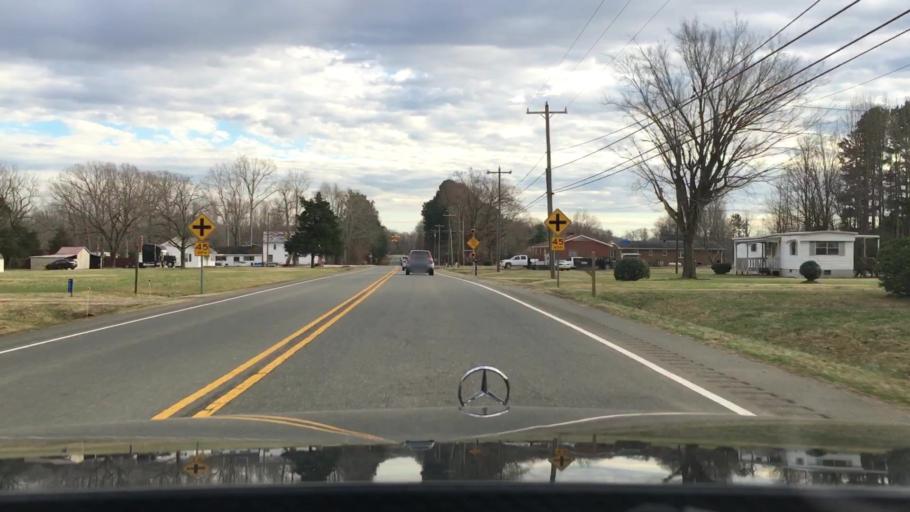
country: US
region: North Carolina
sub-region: Orange County
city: Hillsborough
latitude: 36.1766
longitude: -79.1353
